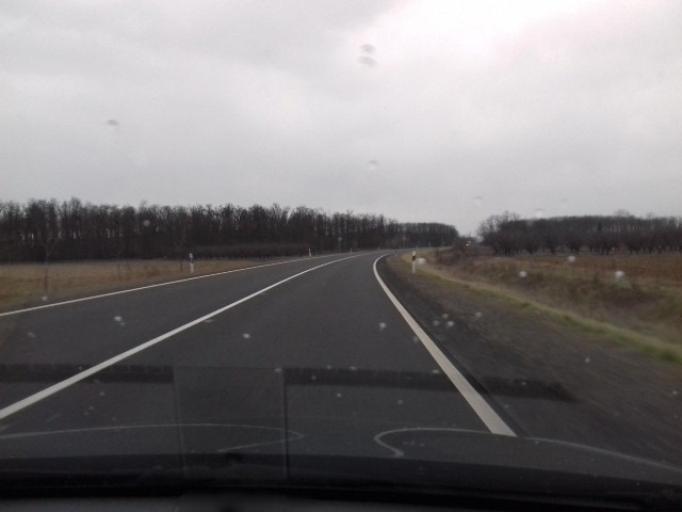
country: HU
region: Szabolcs-Szatmar-Bereg
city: Nyirpazony
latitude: 48.0056
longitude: 21.8427
